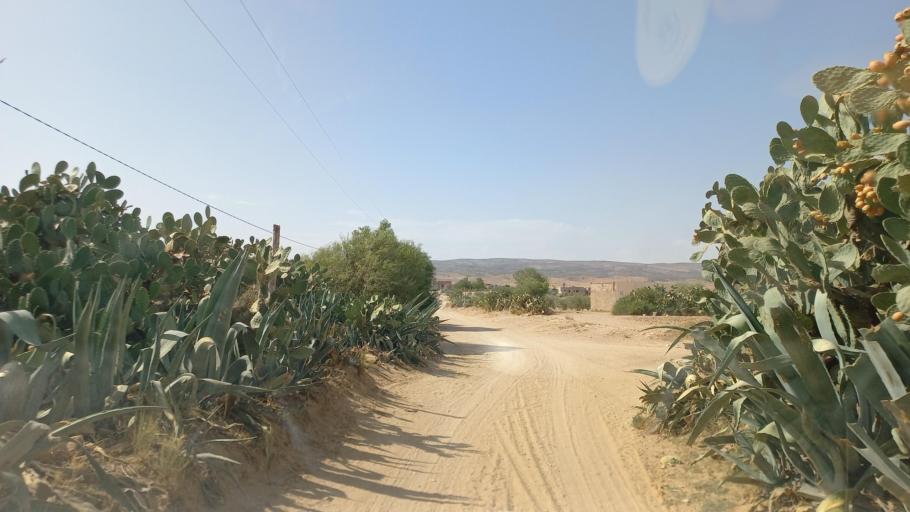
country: TN
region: Al Qasrayn
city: Kasserine
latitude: 35.2734
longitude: 8.9474
